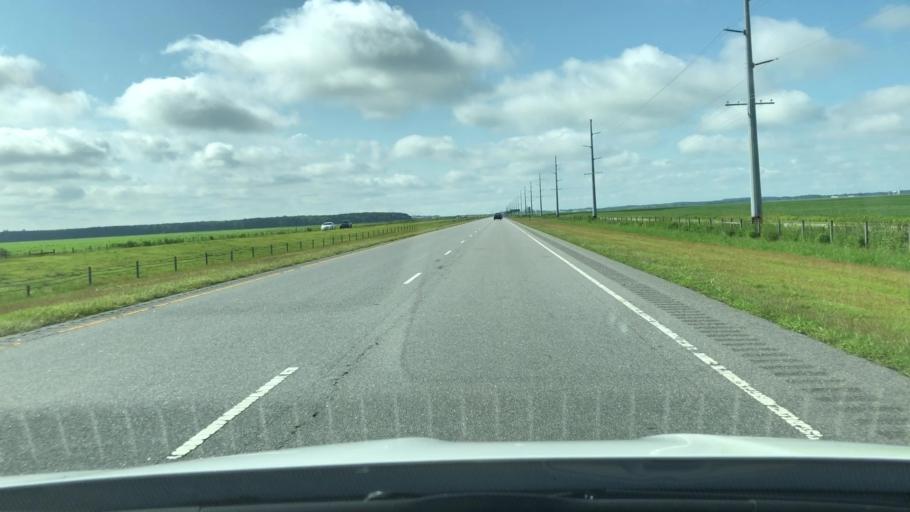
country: US
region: North Carolina
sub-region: Pasquotank County
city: Elizabeth City
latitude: 36.3196
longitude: -76.3092
